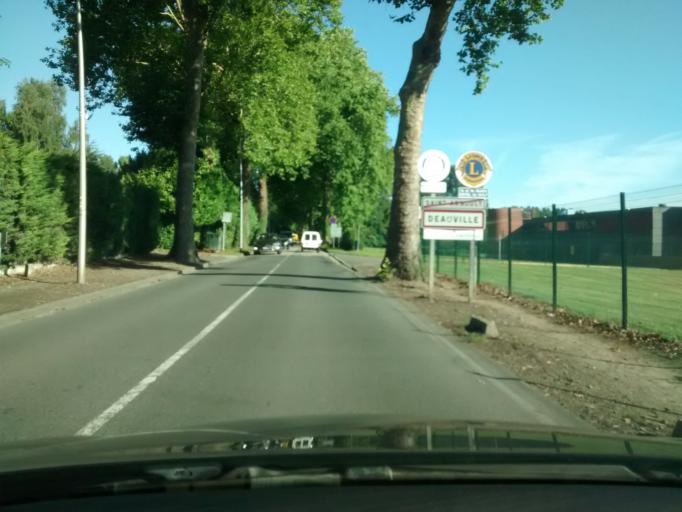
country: FR
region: Lower Normandy
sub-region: Departement du Calvados
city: Deauville
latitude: 49.3460
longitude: 0.0834
